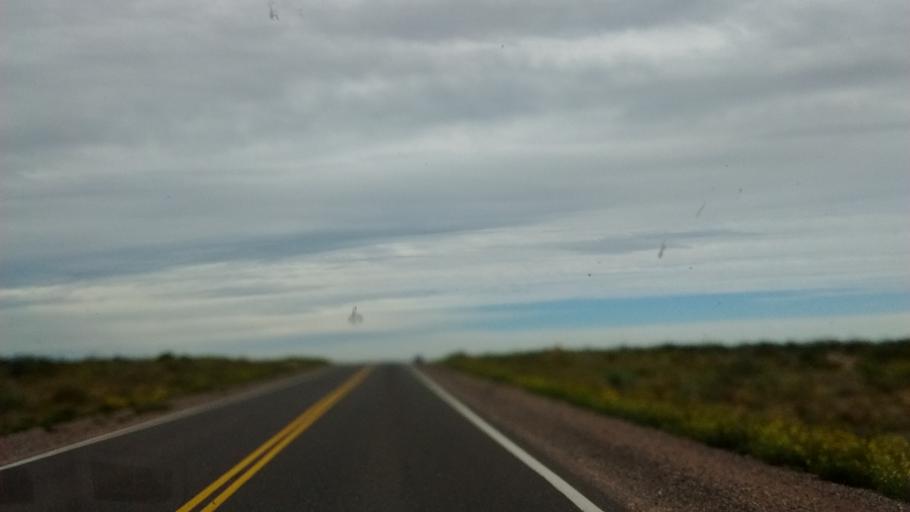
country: AR
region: Rio Negro
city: Catriel
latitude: -38.2551
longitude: -67.9886
